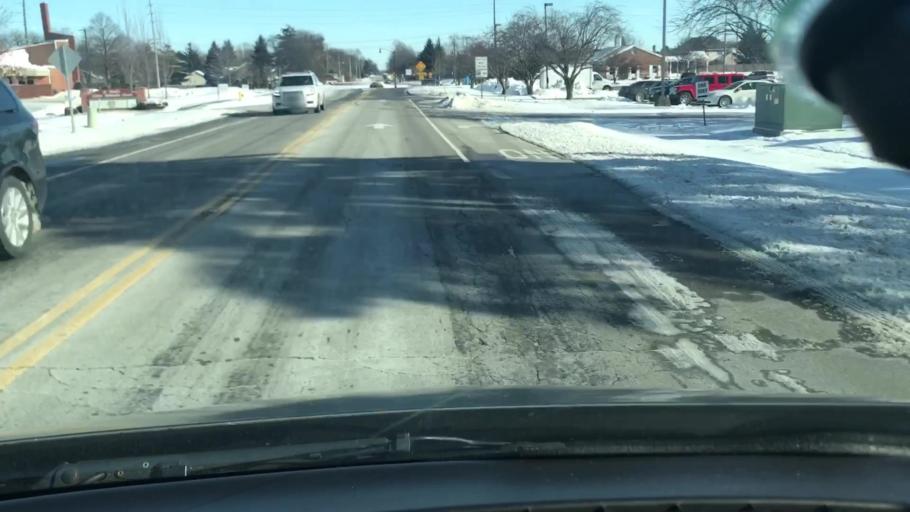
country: US
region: Indiana
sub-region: Hamilton County
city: Carmel
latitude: 39.9712
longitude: -86.0918
